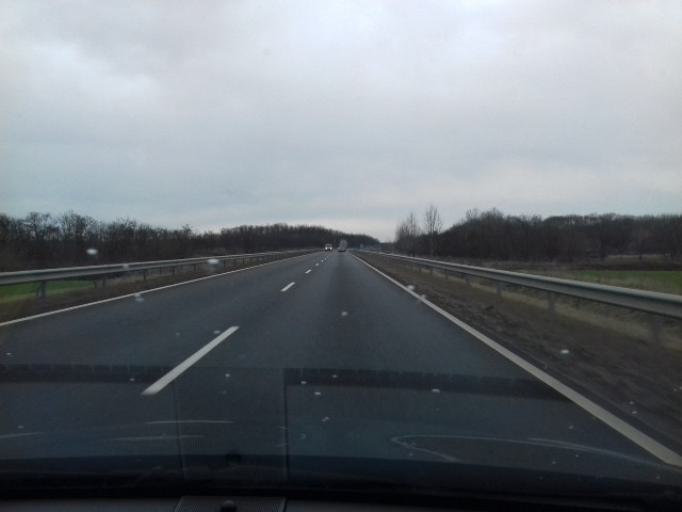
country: HU
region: Szabolcs-Szatmar-Bereg
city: Napkor
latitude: 47.9300
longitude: 21.8193
